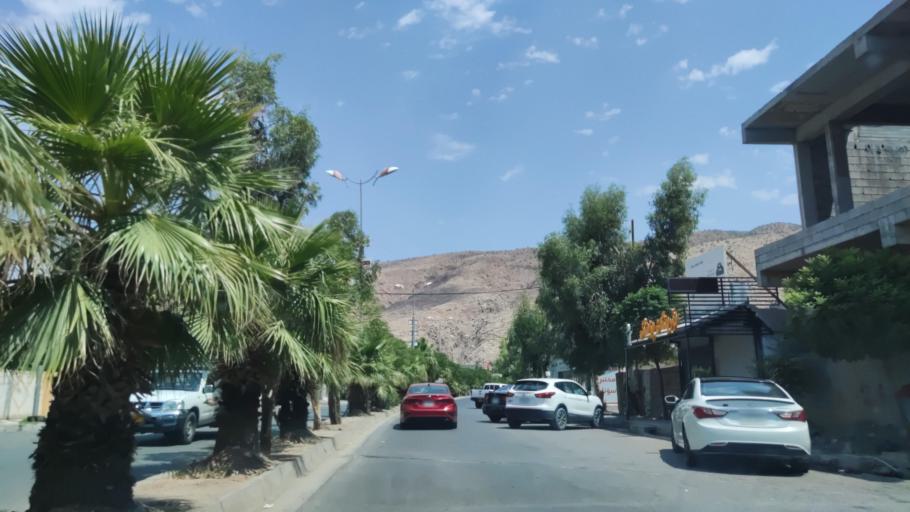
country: IQ
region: Arbil
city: Shaqlawah
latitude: 36.5467
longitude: 44.3492
